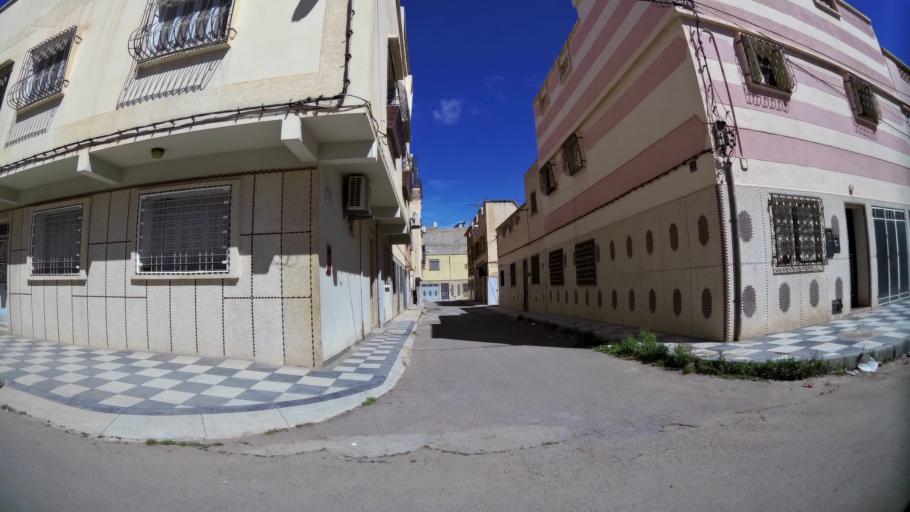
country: MA
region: Oriental
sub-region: Oujda-Angad
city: Oujda
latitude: 34.6684
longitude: -1.9288
